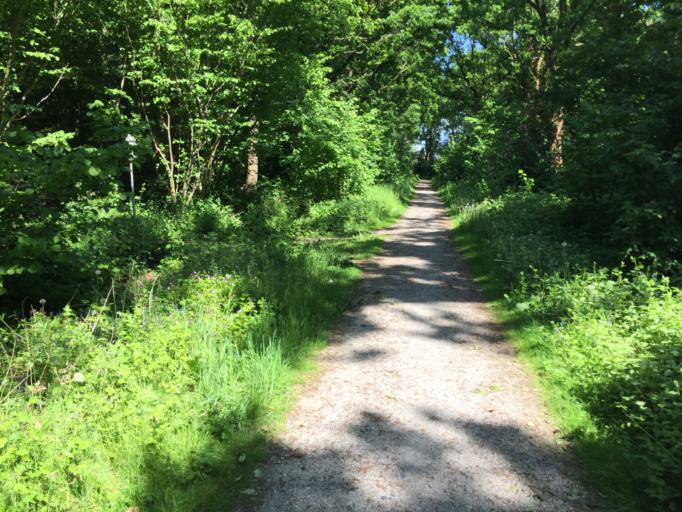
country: NL
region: Friesland
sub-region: Gemeente Heerenveen
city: Jubbega
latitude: 52.9881
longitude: 6.2782
